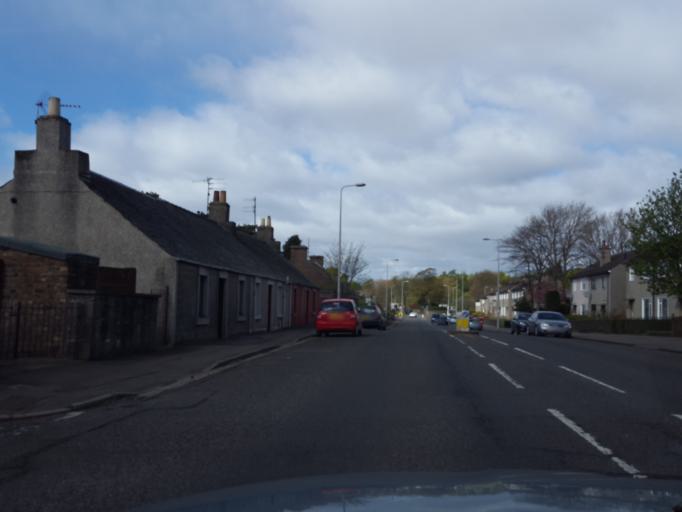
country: GB
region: Scotland
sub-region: Angus
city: Muirhead
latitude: 56.4766
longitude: -3.0247
